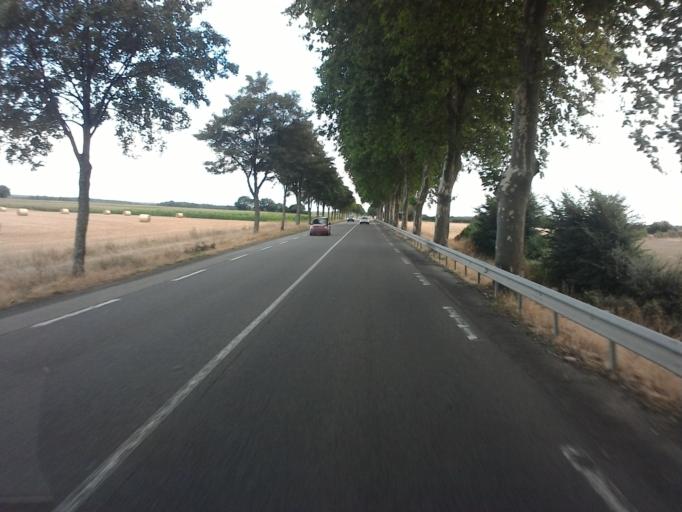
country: FR
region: Rhone-Alpes
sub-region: Departement de l'Ain
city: Saint-Martin-du-Mont
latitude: 46.1015
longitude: 5.3088
